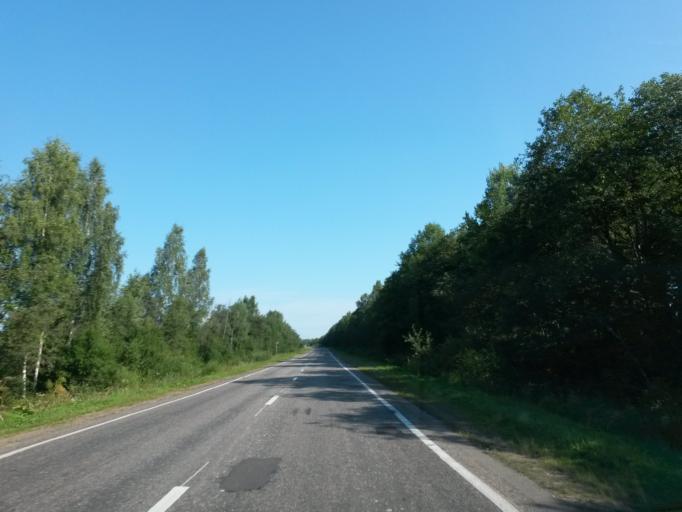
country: RU
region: Jaroslavl
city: Gavrilov-Yam
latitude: 57.4363
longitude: 39.9179
